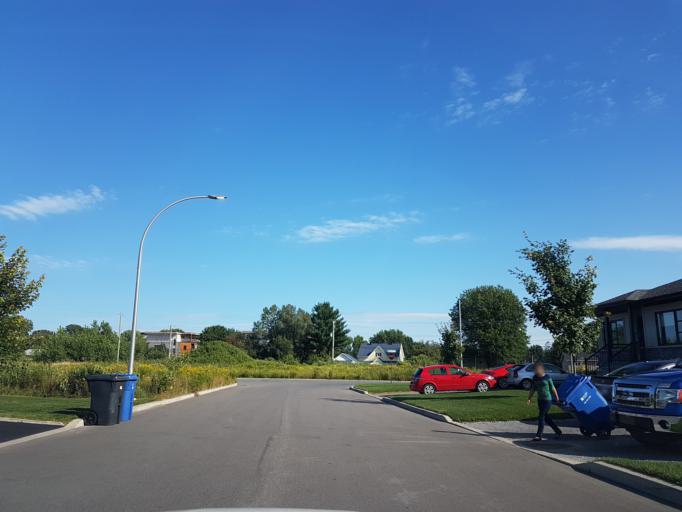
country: CA
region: Quebec
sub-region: Mauricie
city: Nicolet
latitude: 46.2895
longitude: -72.6419
